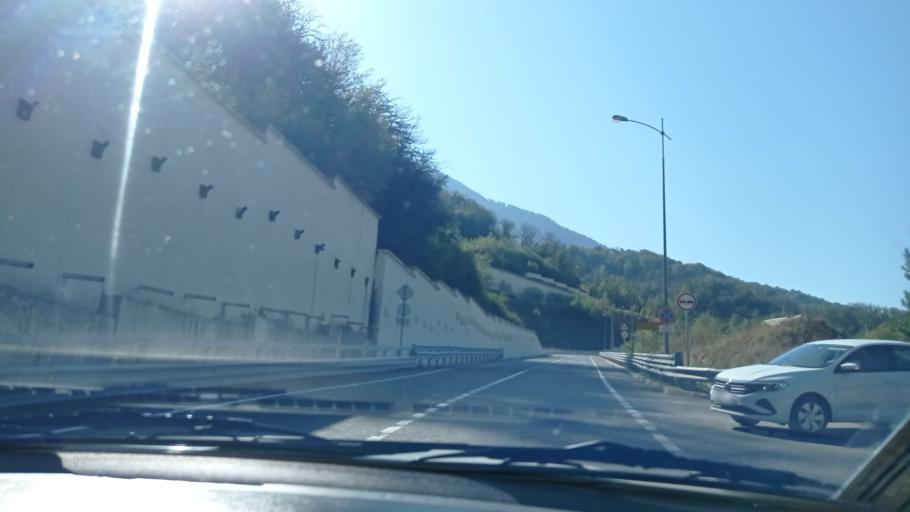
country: RU
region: Krasnodarskiy
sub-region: Sochi City
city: Krasnaya Polyana
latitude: 43.6834
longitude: 40.2457
